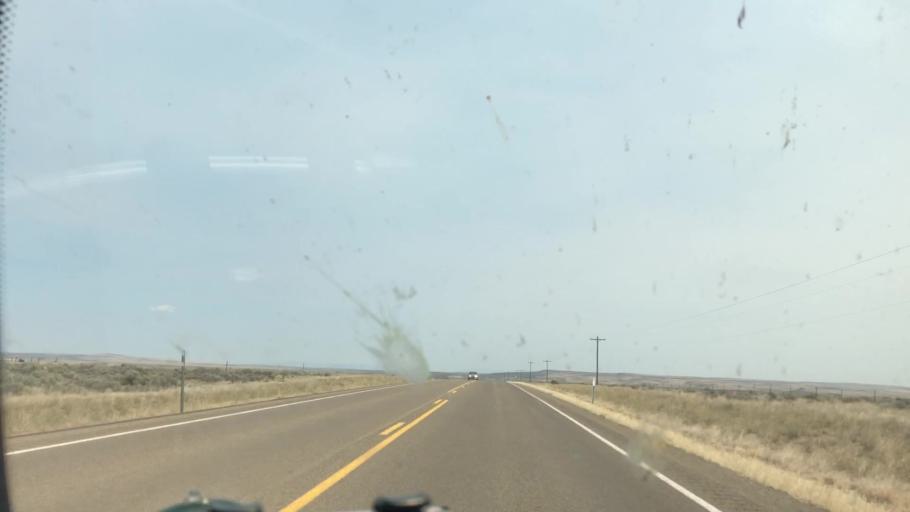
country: US
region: Idaho
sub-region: Owyhee County
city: Homedale
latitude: 42.8577
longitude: -117.5680
